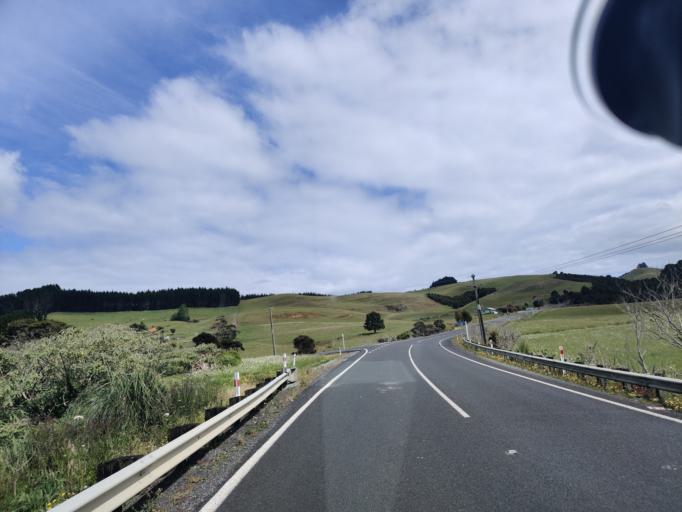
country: NZ
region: Northland
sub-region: Far North District
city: Taipa
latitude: -35.0148
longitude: 173.6246
